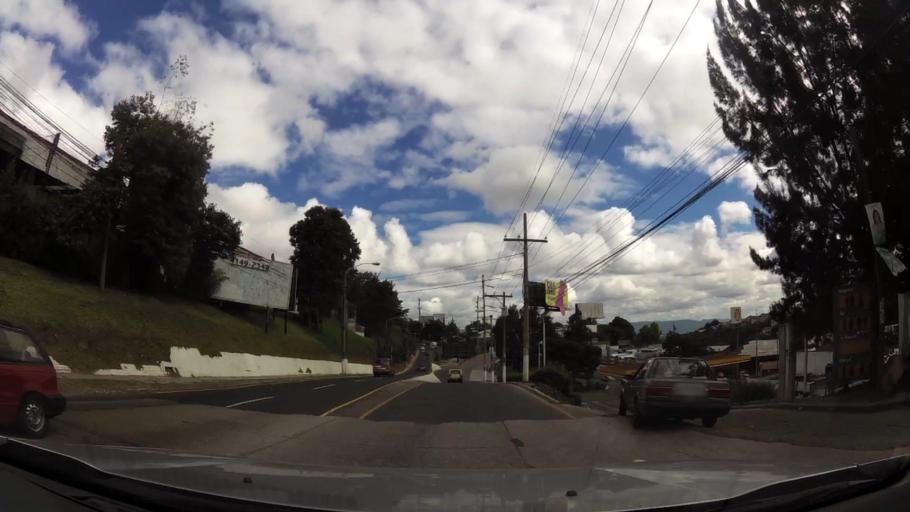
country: GT
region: Guatemala
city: Mixco
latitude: 14.6358
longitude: -90.5988
